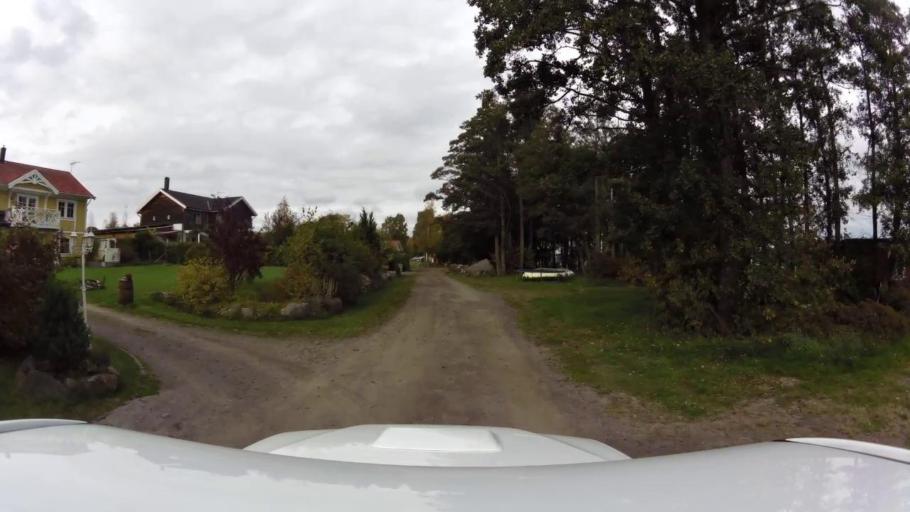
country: SE
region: OEstergoetland
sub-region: Linkopings Kommun
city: Ekangen
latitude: 58.4492
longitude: 15.5871
